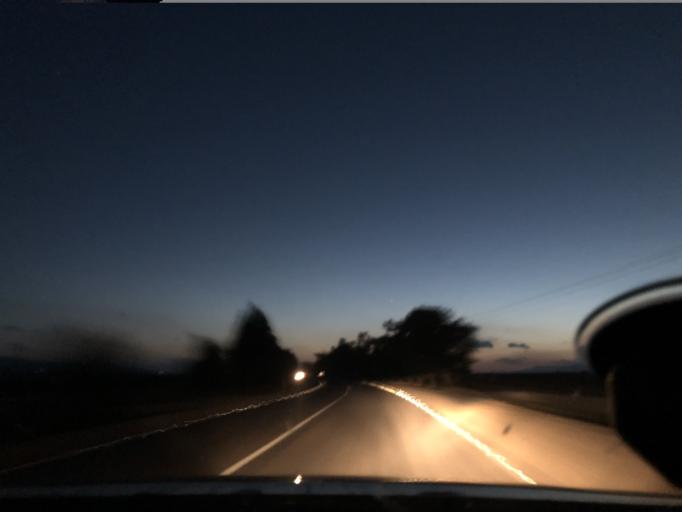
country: TN
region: Al Qasrayn
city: Kasserine
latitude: 35.2490
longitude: 9.0011
